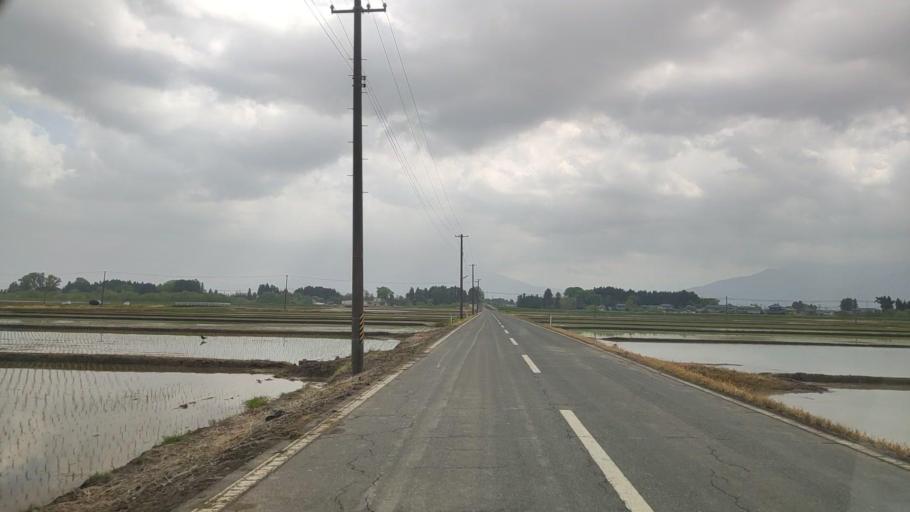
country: JP
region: Niigata
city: Gosen
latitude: 37.7276
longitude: 139.1473
